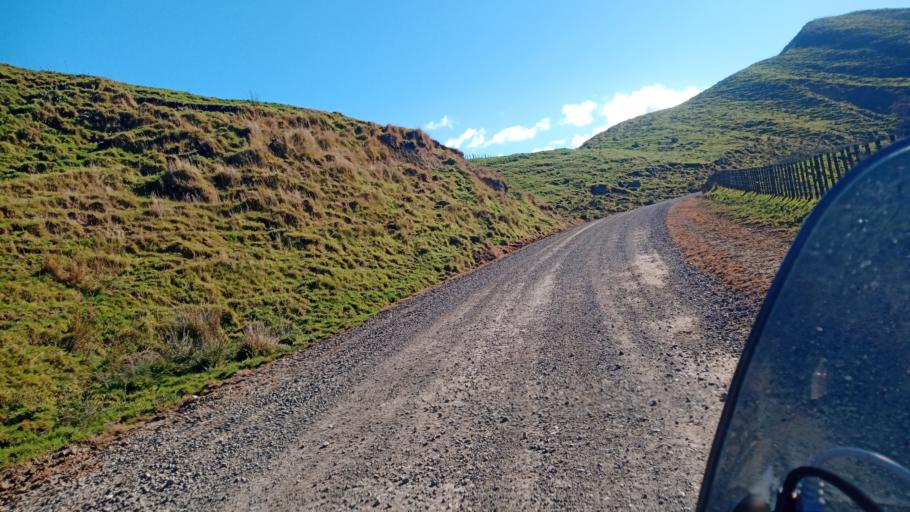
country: NZ
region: Hawke's Bay
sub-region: Wairoa District
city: Wairoa
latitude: -38.7785
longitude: 177.2634
